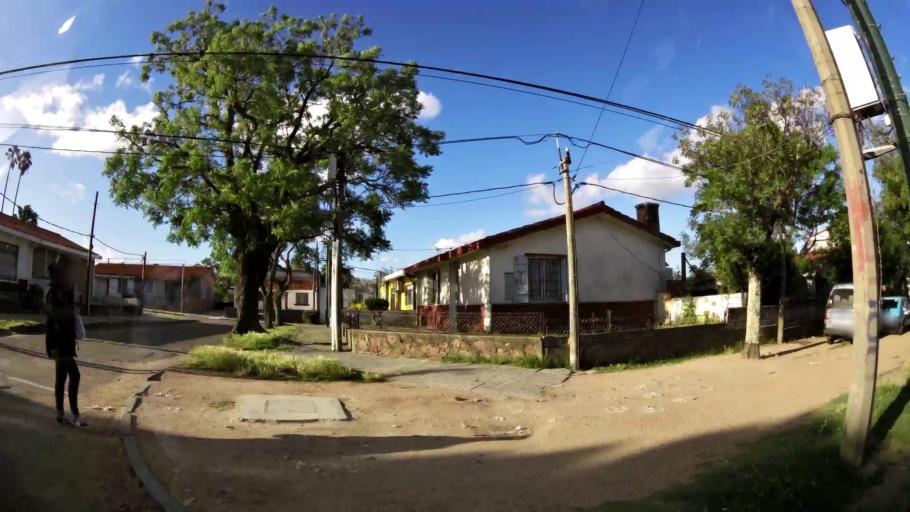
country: UY
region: Montevideo
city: Montevideo
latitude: -34.8744
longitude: -56.2535
